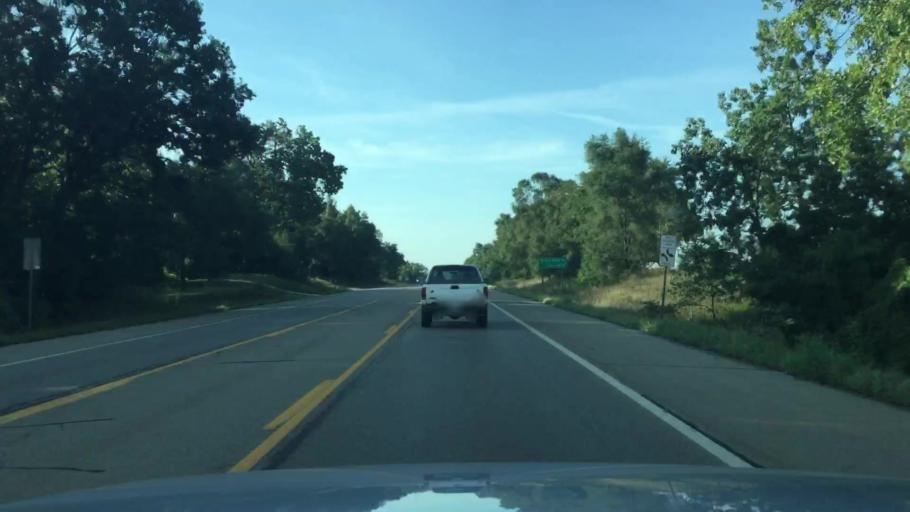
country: US
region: Michigan
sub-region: Jackson County
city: Vandercook Lake
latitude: 42.1713
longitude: -84.3647
